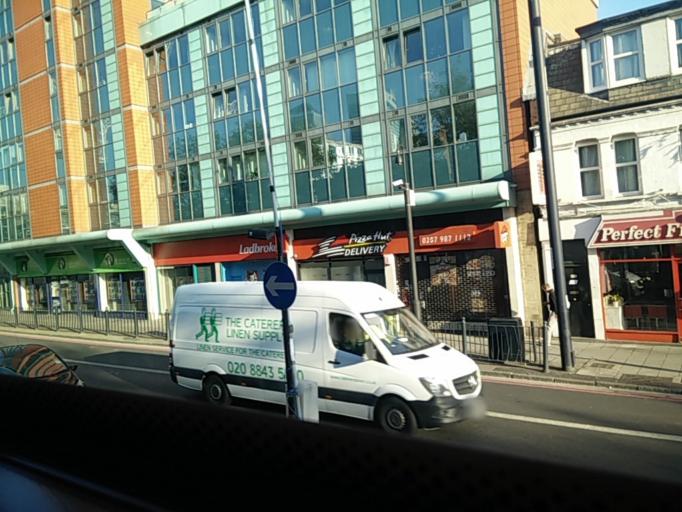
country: GB
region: England
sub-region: Greater London
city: Poplar
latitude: 51.5112
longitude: -0.0123
